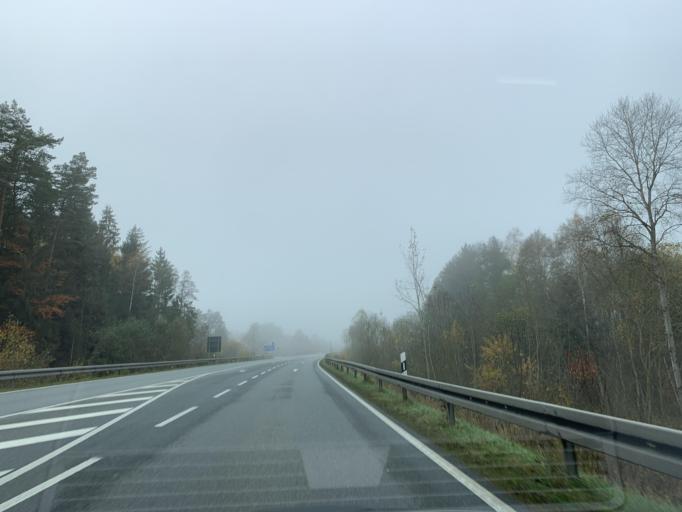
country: DE
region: Bavaria
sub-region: Upper Palatinate
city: Maxhutte-Haidhof
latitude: 49.2185
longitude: 12.1303
